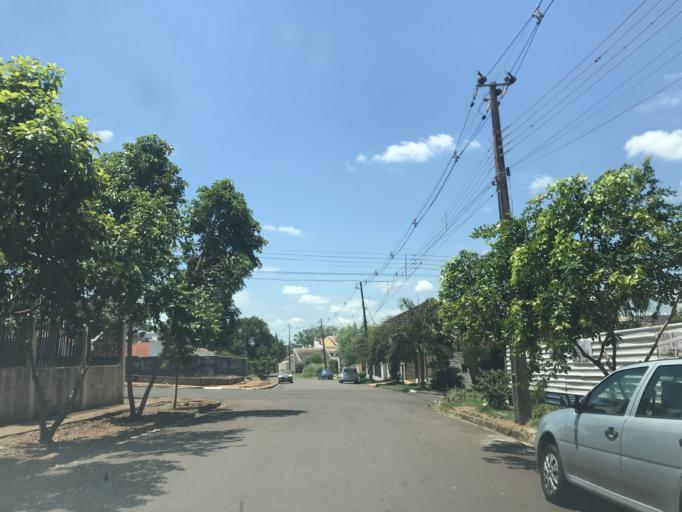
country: BR
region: Parana
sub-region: Maringa
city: Maringa
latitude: -23.4492
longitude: -51.9348
